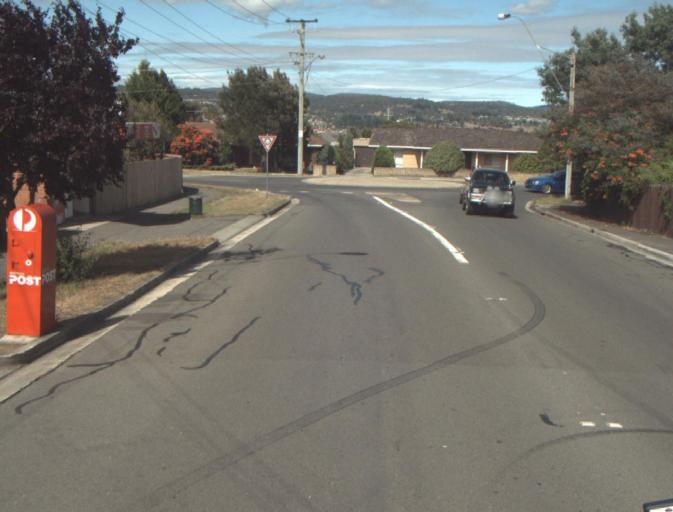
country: AU
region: Tasmania
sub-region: Launceston
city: Mayfield
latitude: -41.3891
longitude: 147.1193
